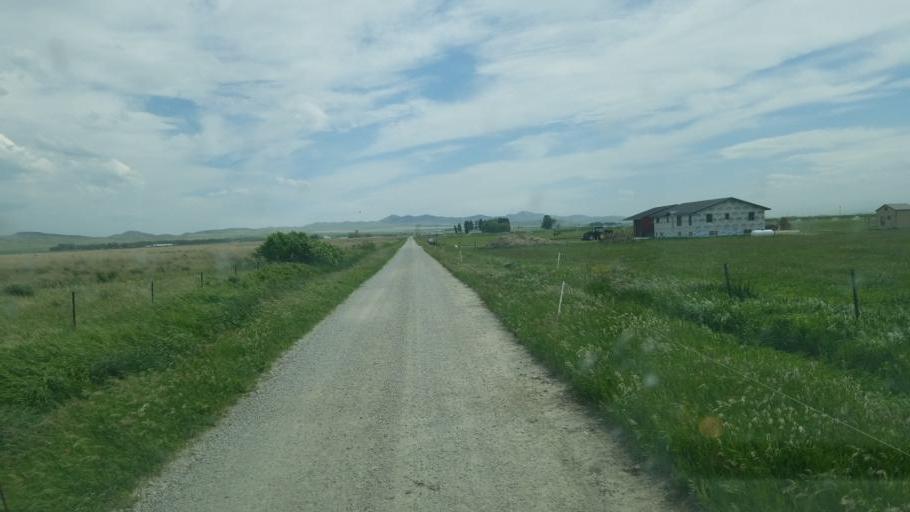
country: US
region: Montana
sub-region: Broadwater County
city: Townsend
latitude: 46.1817
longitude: -111.4720
